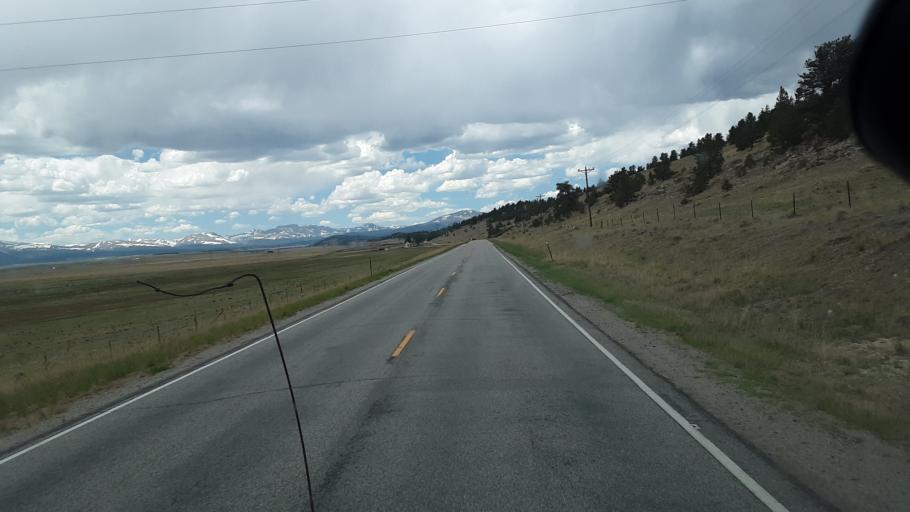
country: US
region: Colorado
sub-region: Park County
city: Fairplay
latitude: 39.0653
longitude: -105.8560
